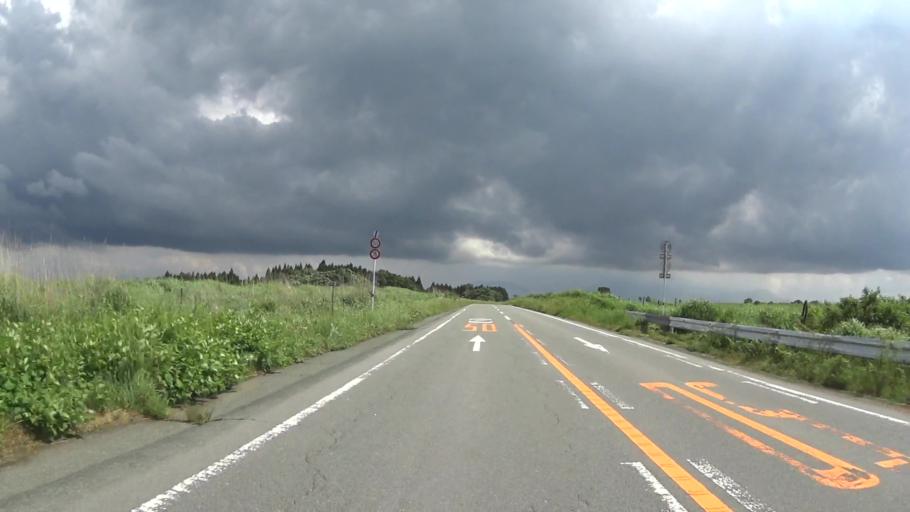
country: JP
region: Kumamoto
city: Aso
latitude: 33.0300
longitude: 131.1625
